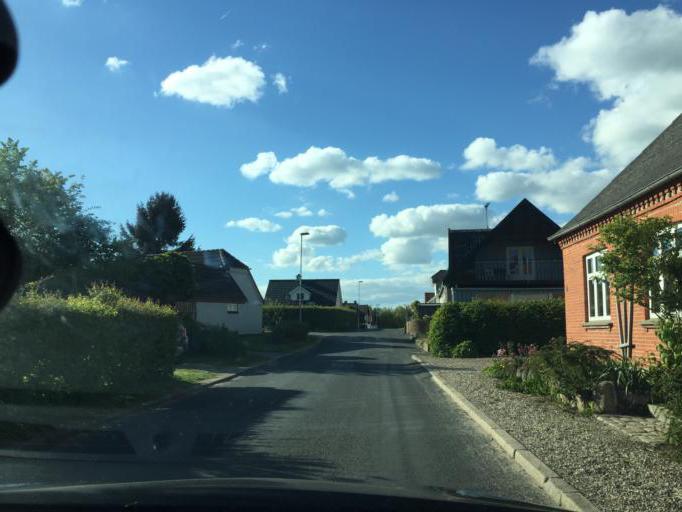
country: DK
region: South Denmark
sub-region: Odense Kommune
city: Bellinge
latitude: 55.3608
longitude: 10.2749
